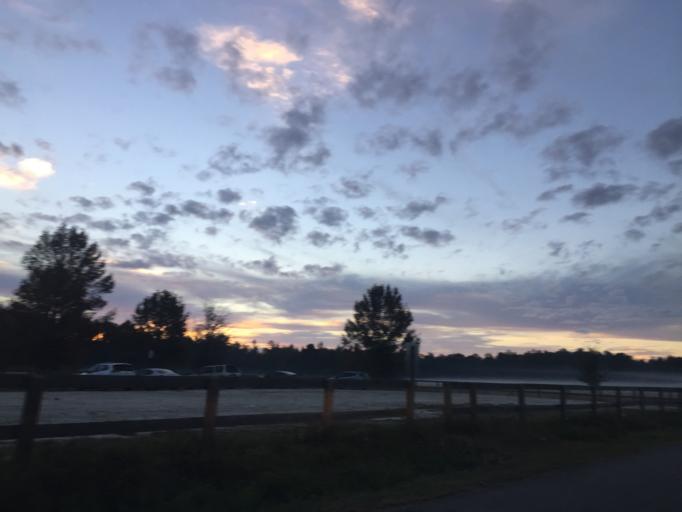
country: US
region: Florida
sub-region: Seminole County
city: Oviedo
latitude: 28.6873
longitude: -81.1597
